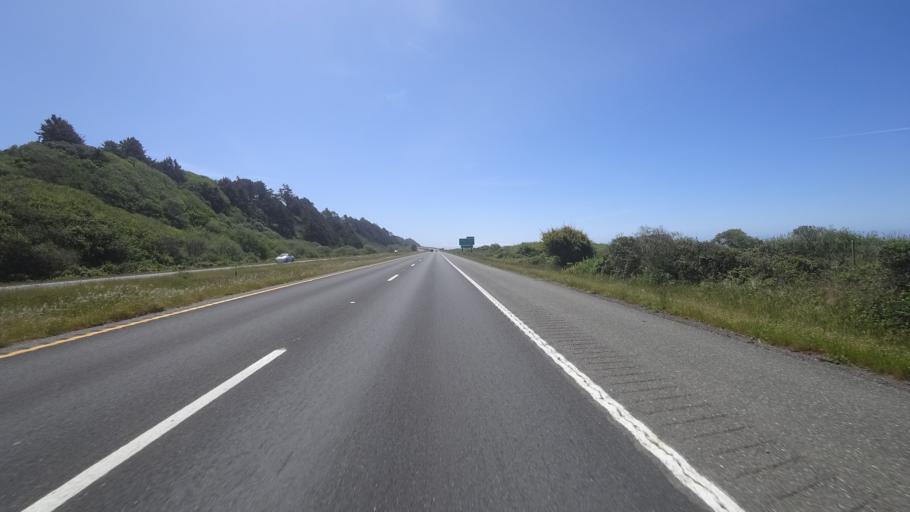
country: US
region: California
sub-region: Humboldt County
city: McKinleyville
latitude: 40.9856
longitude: -124.1164
